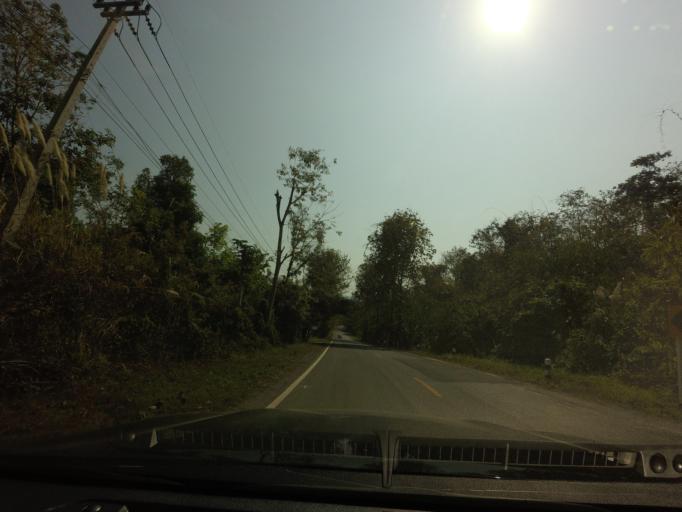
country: TH
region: Kanchanaburi
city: Thong Pha Phum
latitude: 14.6543
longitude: 98.5446
